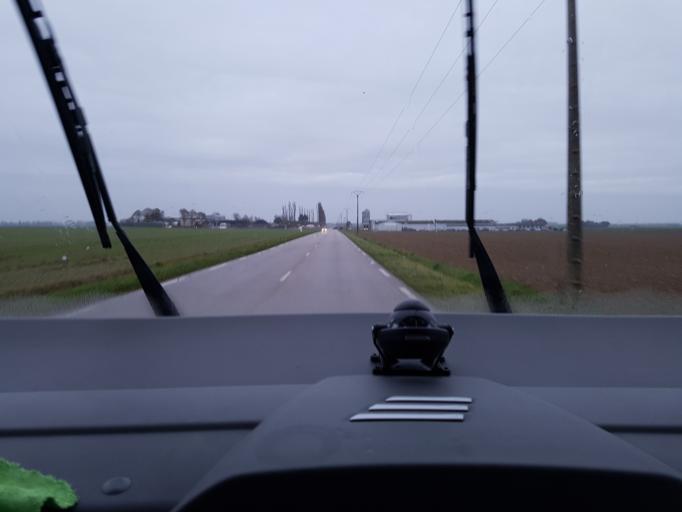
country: FR
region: Haute-Normandie
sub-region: Departement de l'Eure
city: Le Neubourg
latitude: 49.1482
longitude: 0.9310
